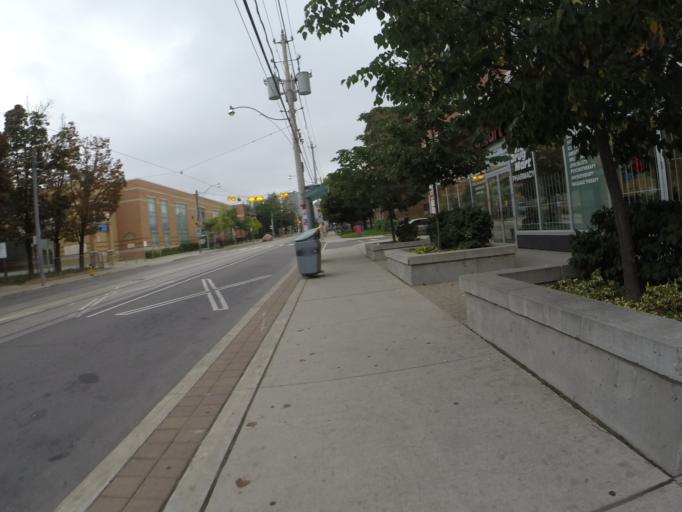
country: CA
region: Ontario
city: Toronto
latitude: 43.6592
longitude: -79.3658
